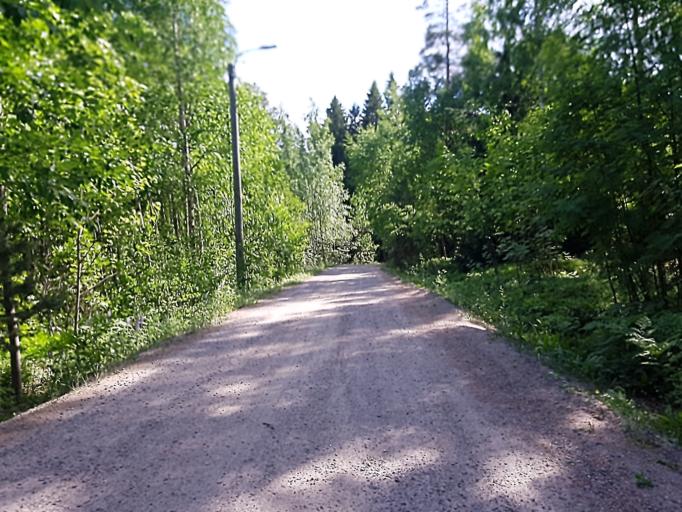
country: FI
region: Uusimaa
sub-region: Helsinki
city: Vantaa
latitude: 60.2944
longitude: 24.9177
